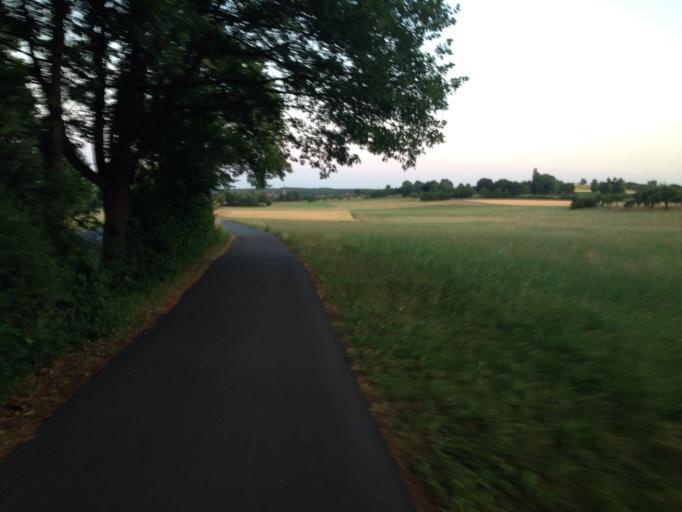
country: DE
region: Hesse
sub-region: Regierungsbezirk Giessen
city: Grossen Buseck
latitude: 50.5661
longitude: 8.7700
